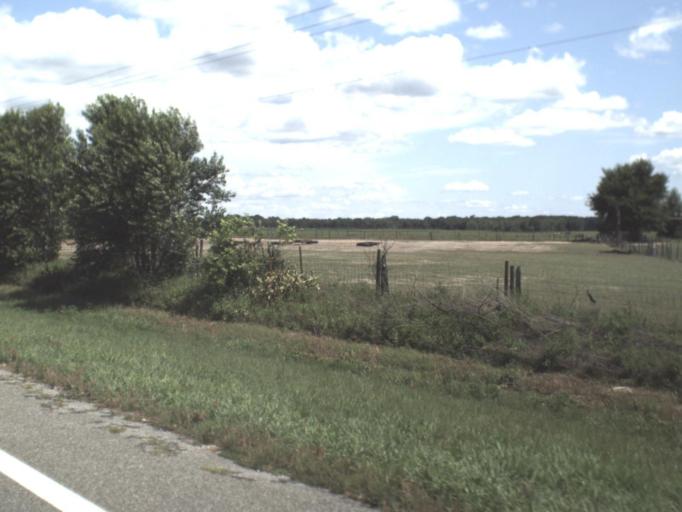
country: US
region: Florida
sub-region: Lafayette County
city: Mayo
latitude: 29.9859
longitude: -83.0015
